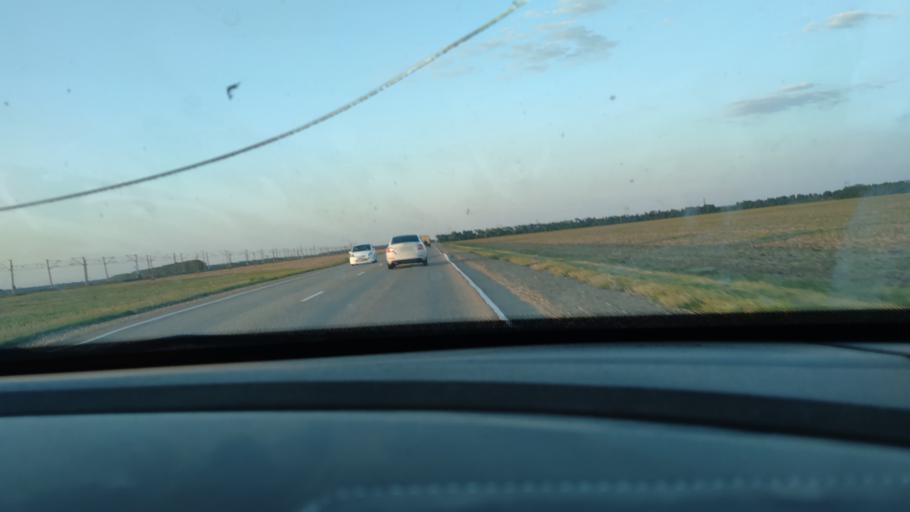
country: RU
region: Krasnodarskiy
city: Novominskaya
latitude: 46.3830
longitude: 38.9841
